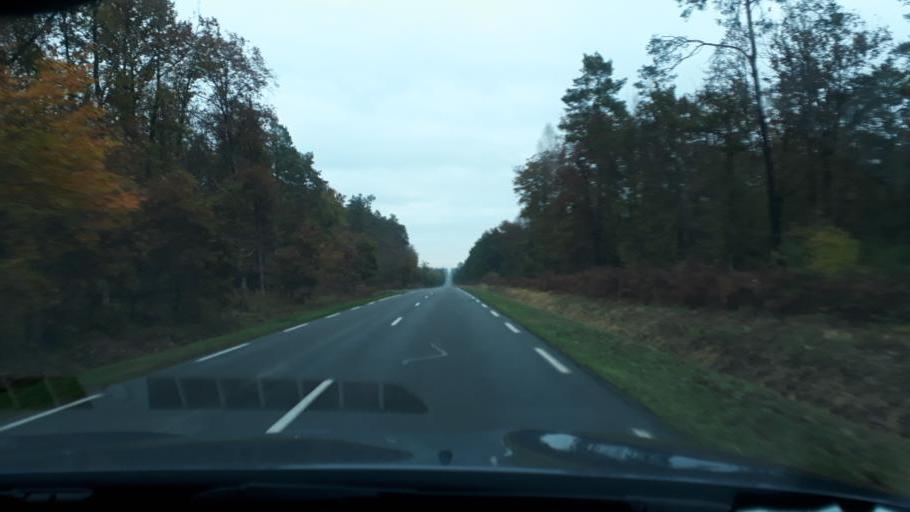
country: FR
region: Centre
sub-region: Departement du Loiret
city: Bouzy-la-Foret
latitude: 47.8356
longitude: 2.4288
